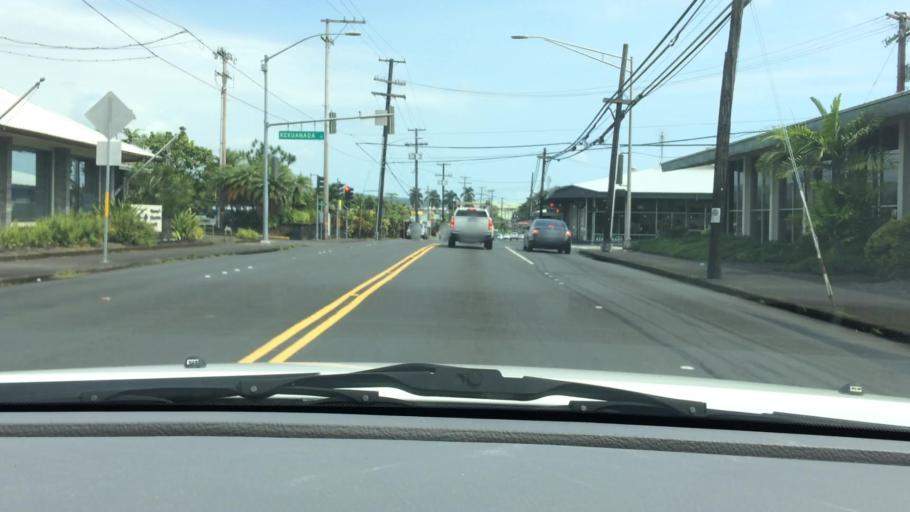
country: US
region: Hawaii
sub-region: Hawaii County
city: Hilo
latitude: 19.7109
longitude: -155.0766
